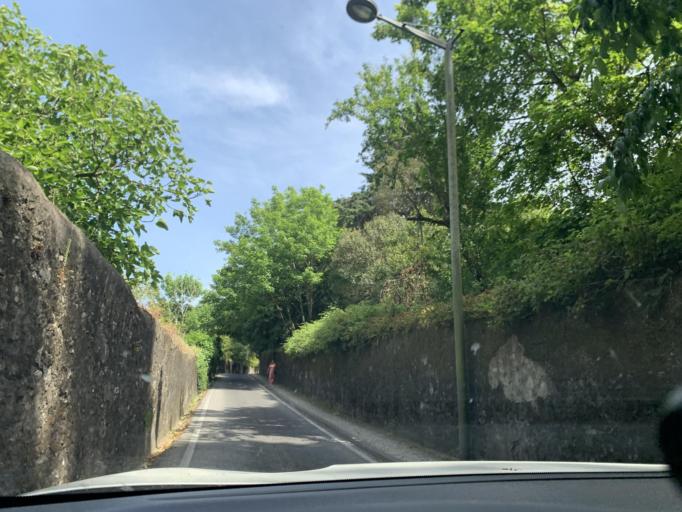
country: PT
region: Lisbon
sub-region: Sintra
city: Sintra
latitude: 38.8026
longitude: -9.3885
